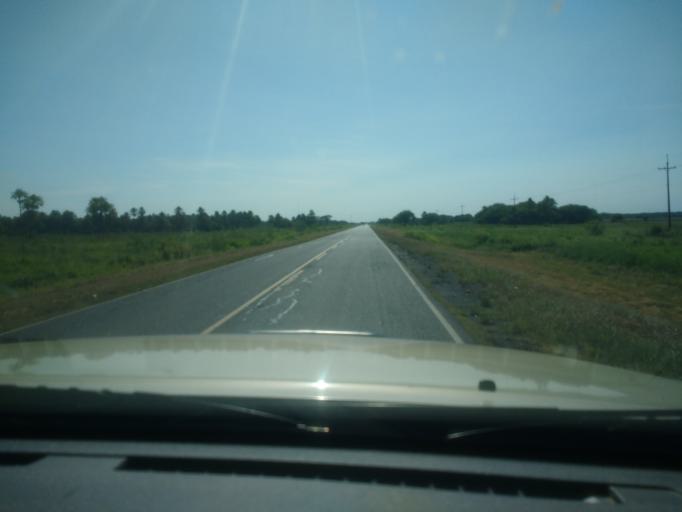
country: PY
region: Presidente Hayes
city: Benjamin Aceval
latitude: -24.9206
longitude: -57.5980
